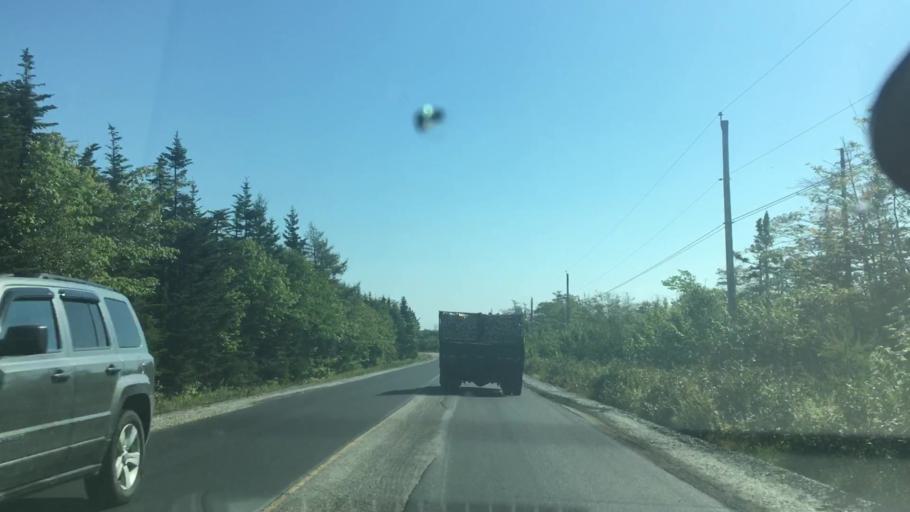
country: CA
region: Nova Scotia
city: New Glasgow
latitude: 44.8987
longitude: -62.4339
